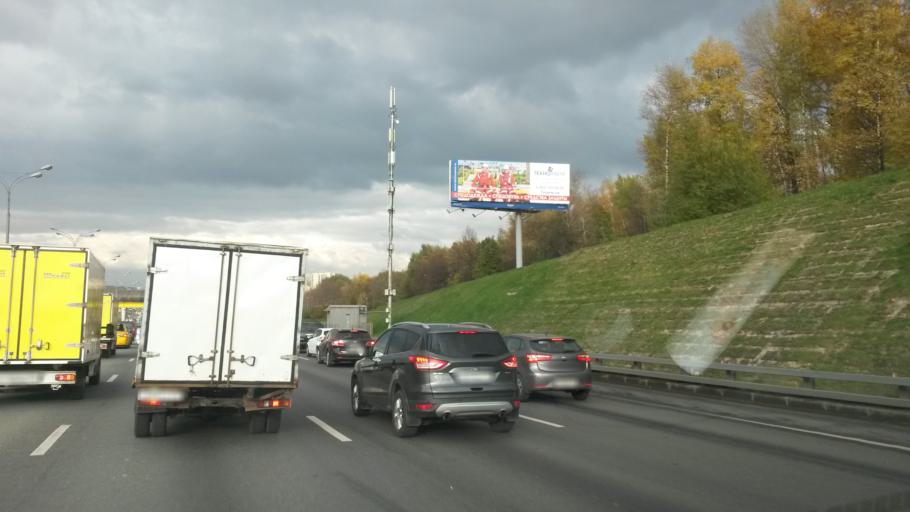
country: RU
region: Moscow
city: Strogino
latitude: 55.8171
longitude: 37.3912
